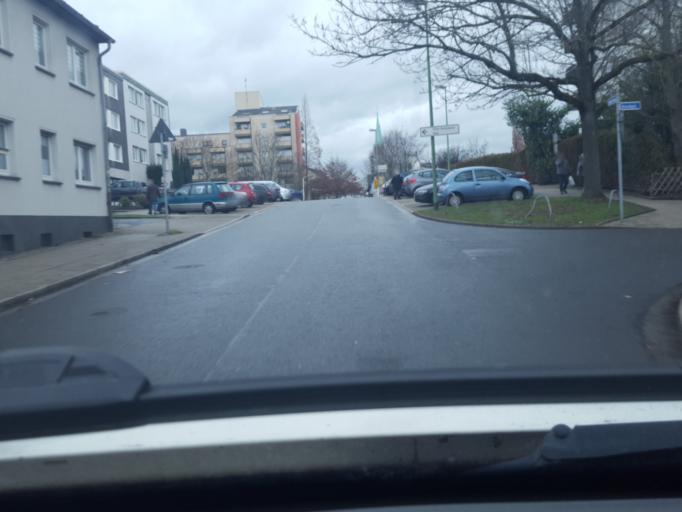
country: DE
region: North Rhine-Westphalia
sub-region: Regierungsbezirk Munster
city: Bottrop
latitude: 51.4712
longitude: 6.9524
